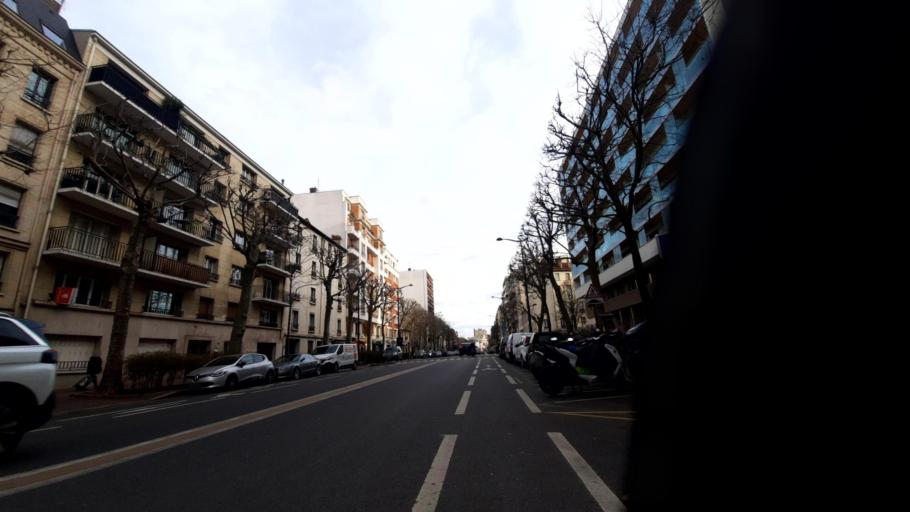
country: FR
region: Ile-de-France
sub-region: Departement du Val-de-Marne
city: Charenton-le-Pont
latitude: 48.8235
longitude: 2.4106
